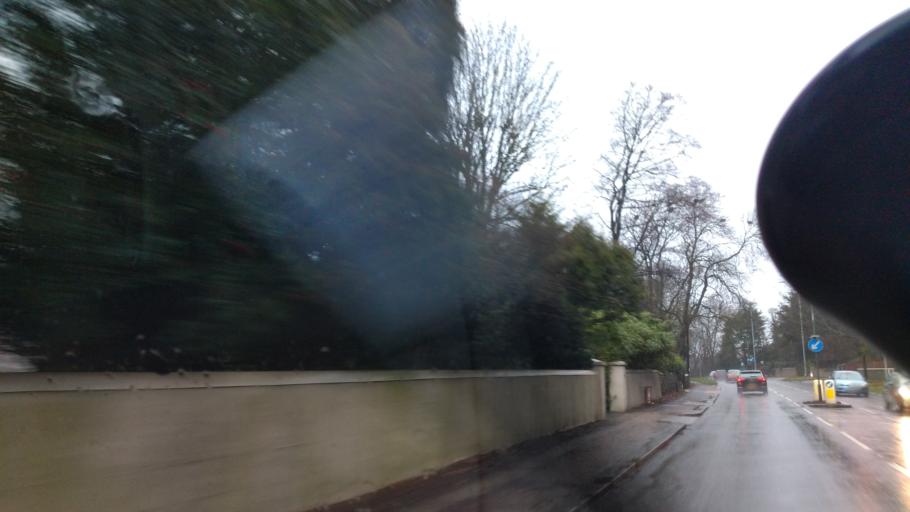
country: GB
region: England
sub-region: West Sussex
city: Broadwater
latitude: 50.8373
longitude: -0.3874
